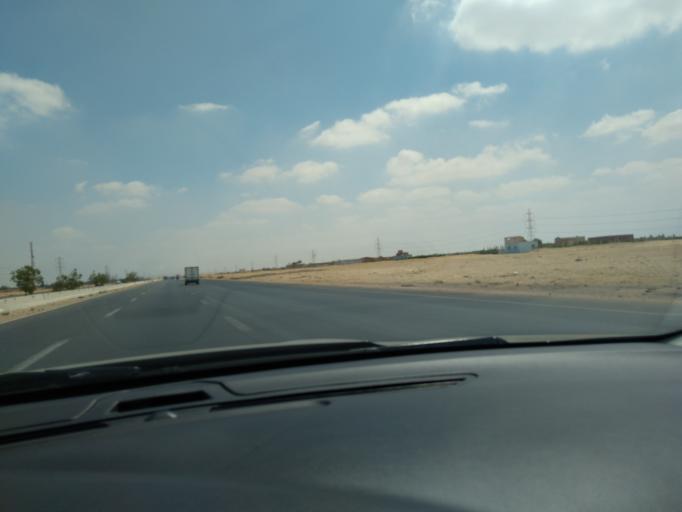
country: EG
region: Al Isma'iliyah
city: At Tall al Kabir
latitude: 30.3499
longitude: 31.8836
